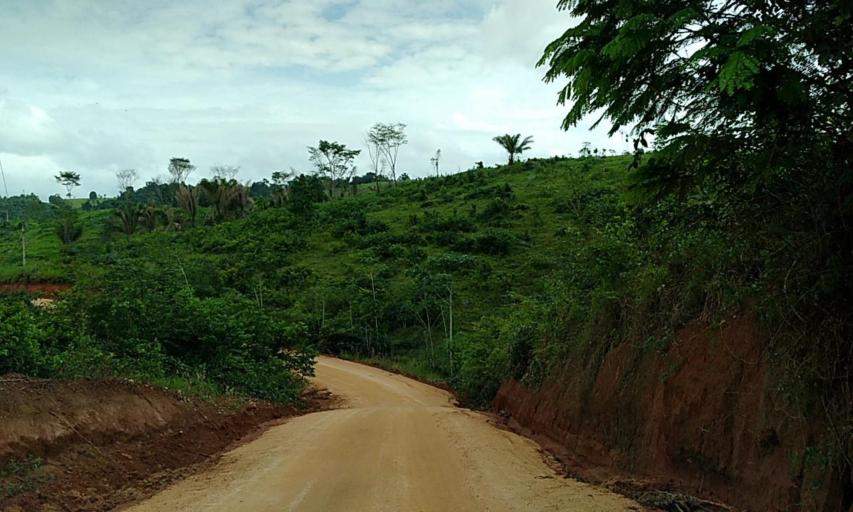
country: BR
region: Para
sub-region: Senador Jose Porfirio
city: Senador Jose Porfirio
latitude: -3.0802
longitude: -51.6344
